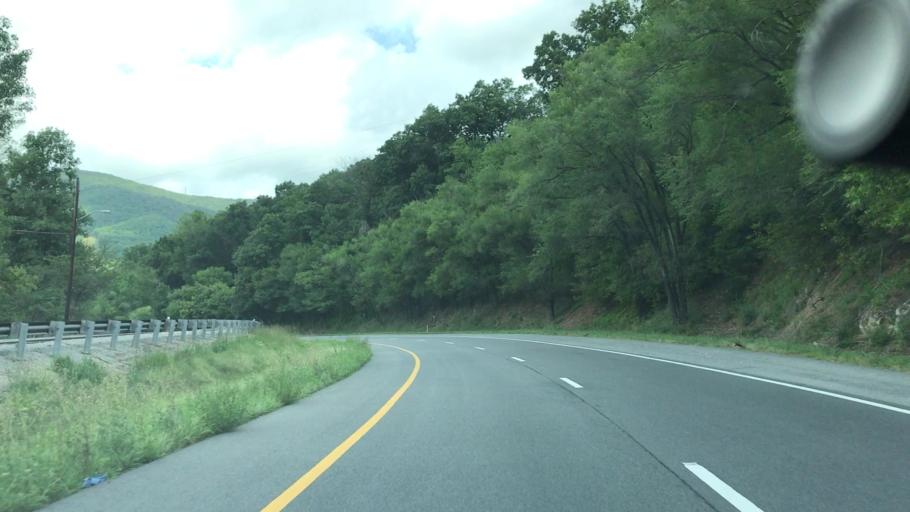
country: US
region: Virginia
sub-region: Giles County
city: Pearisburg
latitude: 37.3455
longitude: -80.7592
